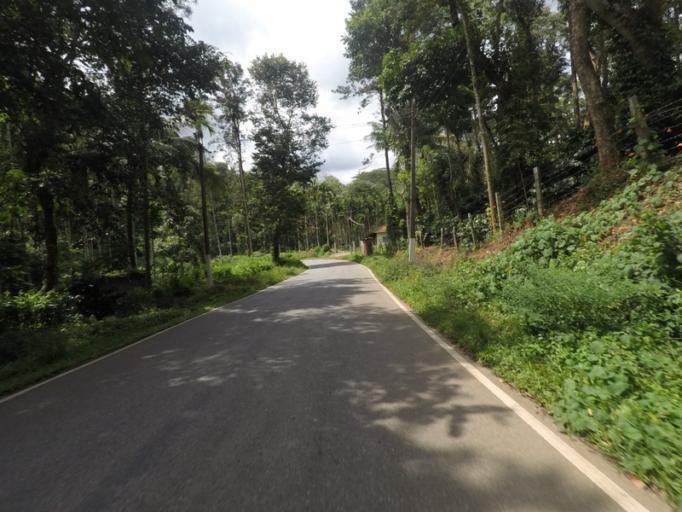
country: IN
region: Karnataka
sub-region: Kodagu
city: Suntikoppa
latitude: 12.3412
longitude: 75.8656
